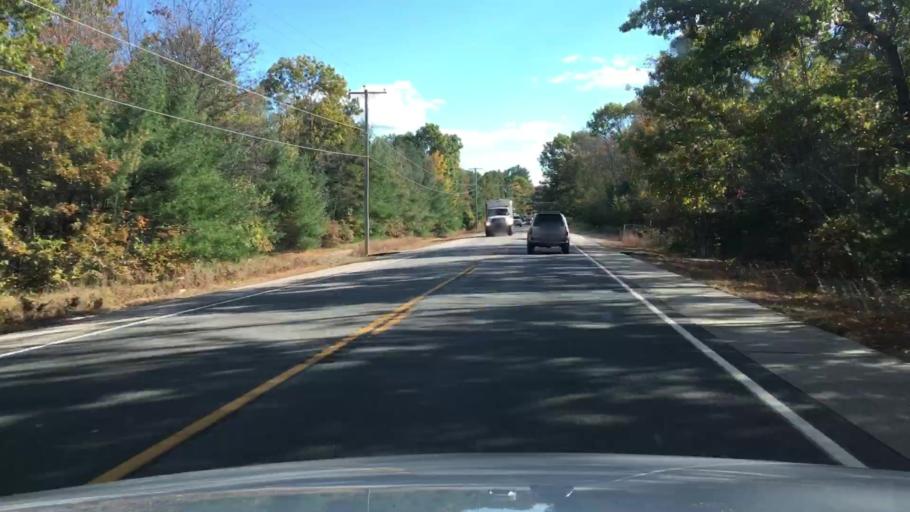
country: US
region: Maine
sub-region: York County
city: South Sanford
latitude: 43.3869
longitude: -70.6902
